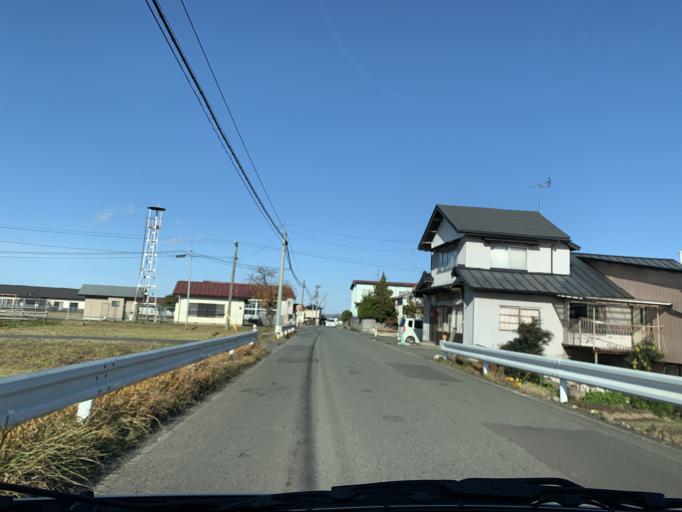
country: JP
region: Iwate
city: Mizusawa
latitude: 39.1598
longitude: 141.0984
